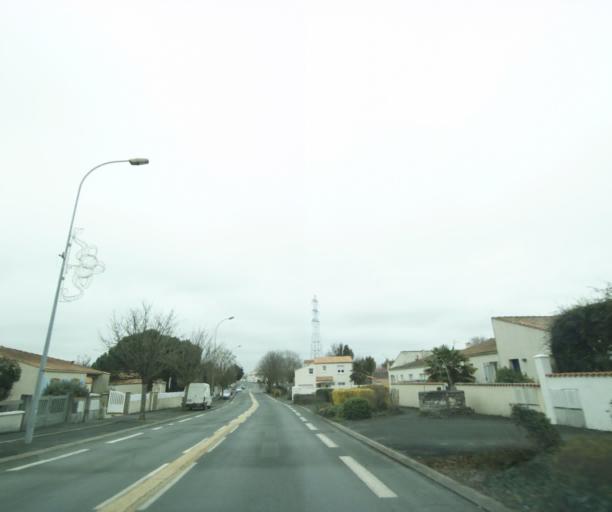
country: FR
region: Poitou-Charentes
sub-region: Departement de la Charente-Maritime
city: Lagord
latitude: 46.1836
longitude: -1.1419
